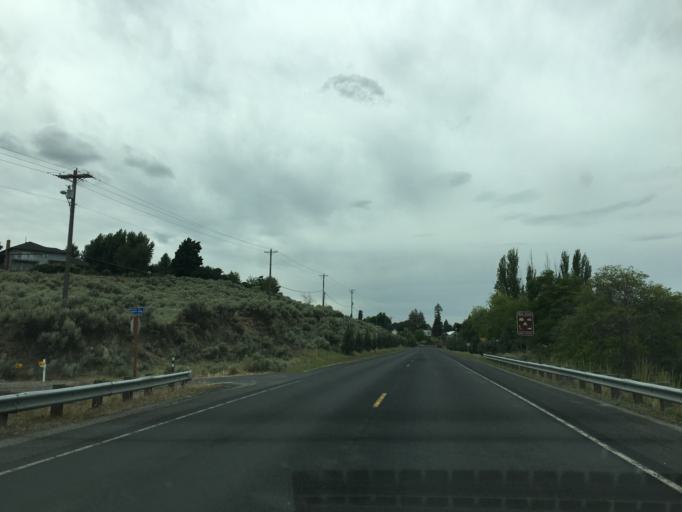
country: US
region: Washington
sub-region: Okanogan County
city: Coulee Dam
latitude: 47.9357
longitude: -119.0243
